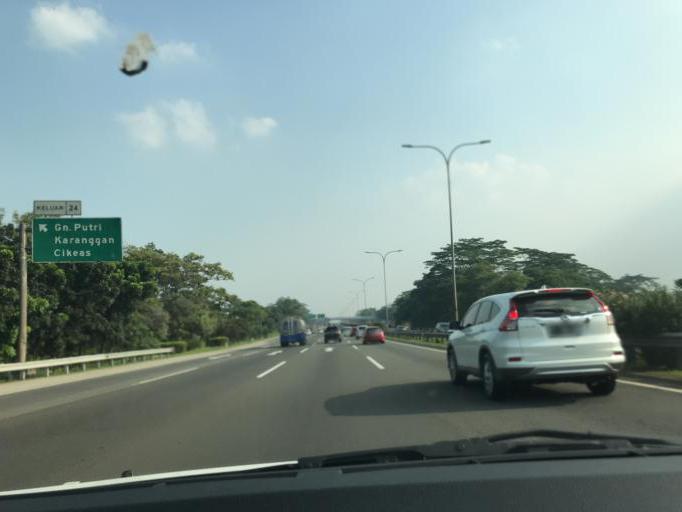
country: ID
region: West Java
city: Citeureup
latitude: -6.4536
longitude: 106.8888
